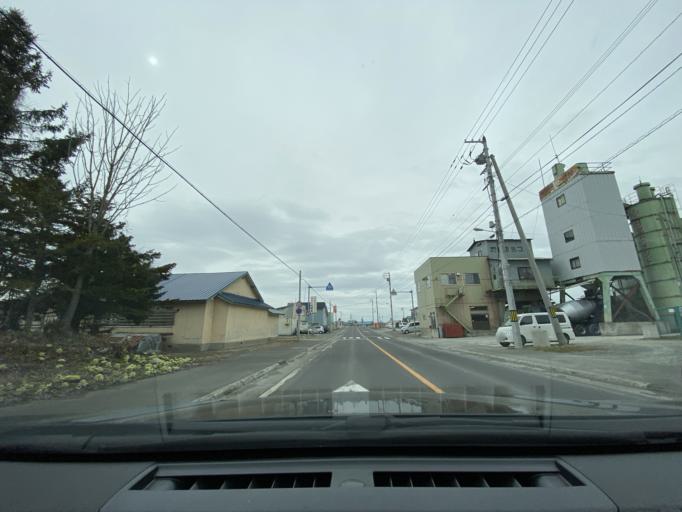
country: JP
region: Hokkaido
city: Nayoro
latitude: 44.1367
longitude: 142.4819
